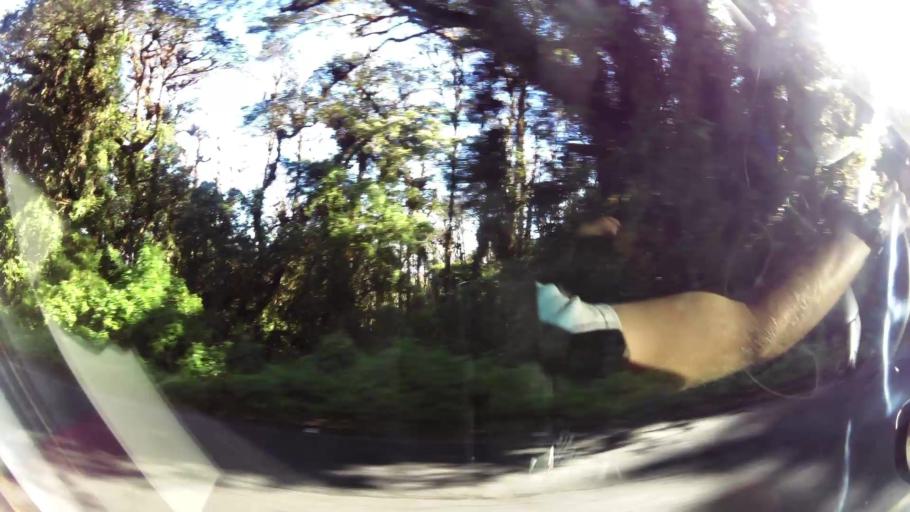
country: CR
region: San Jose
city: San Marcos
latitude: 9.6988
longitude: -83.9341
